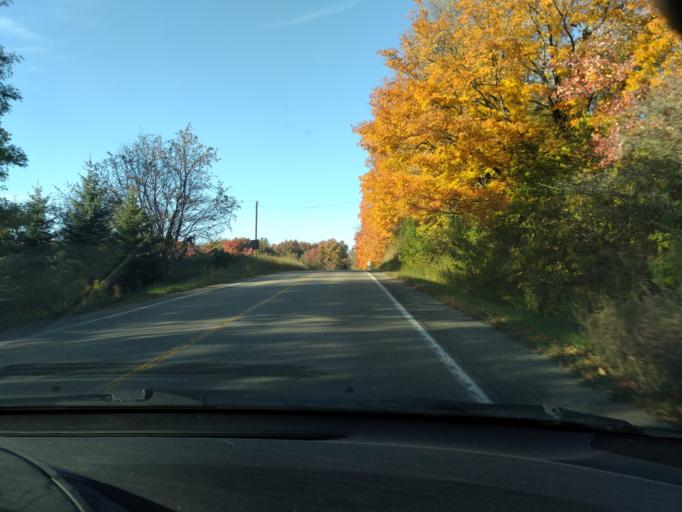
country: CA
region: Ontario
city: Bradford West Gwillimbury
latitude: 43.9569
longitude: -79.7169
